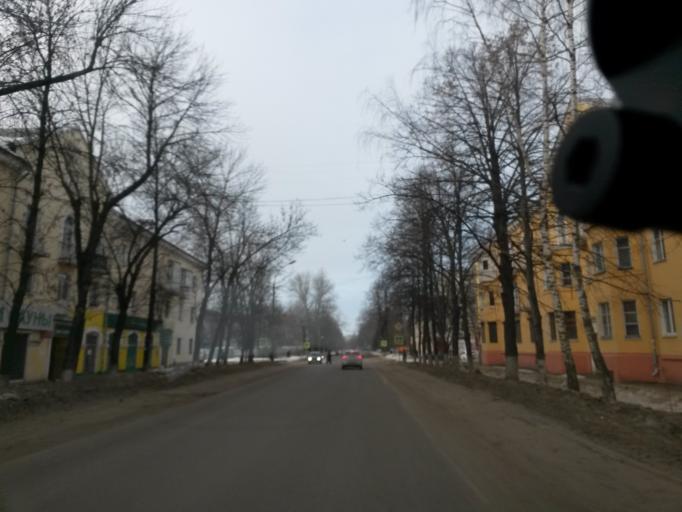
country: RU
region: Jaroslavl
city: Yaroslavl
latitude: 57.6343
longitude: 39.8452
